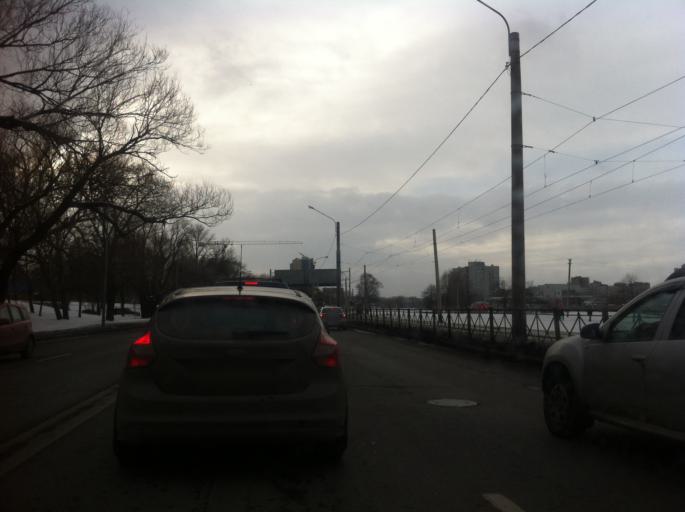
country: RU
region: St.-Petersburg
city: Dachnoye
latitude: 59.8491
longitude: 30.2299
